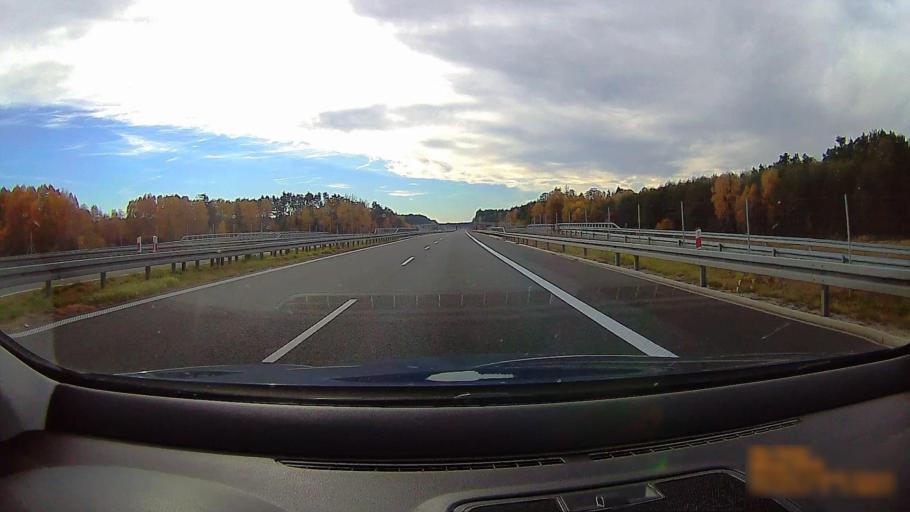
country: PL
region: Greater Poland Voivodeship
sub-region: Powiat ostrowski
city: Przygodzice
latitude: 51.5707
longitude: 17.8483
